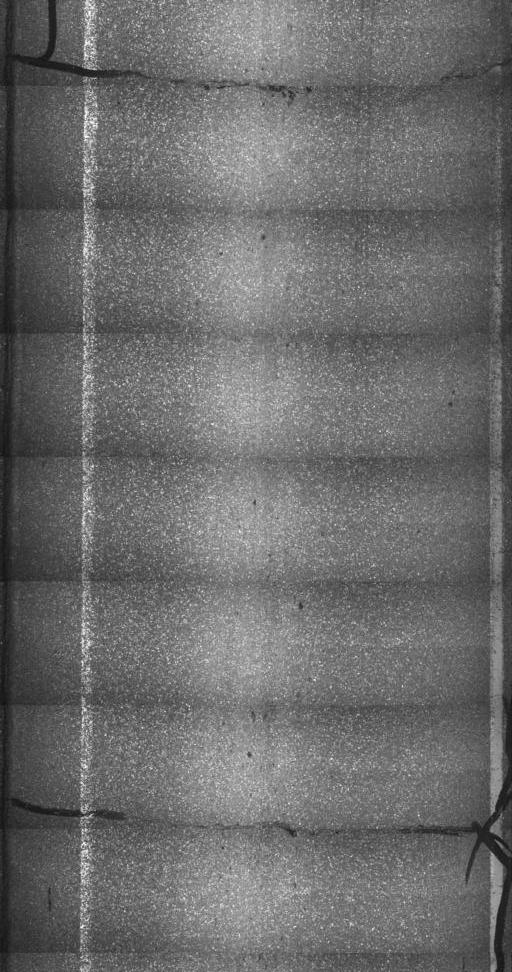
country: US
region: Vermont
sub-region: Washington County
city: Barre
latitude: 44.2268
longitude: -72.4893
